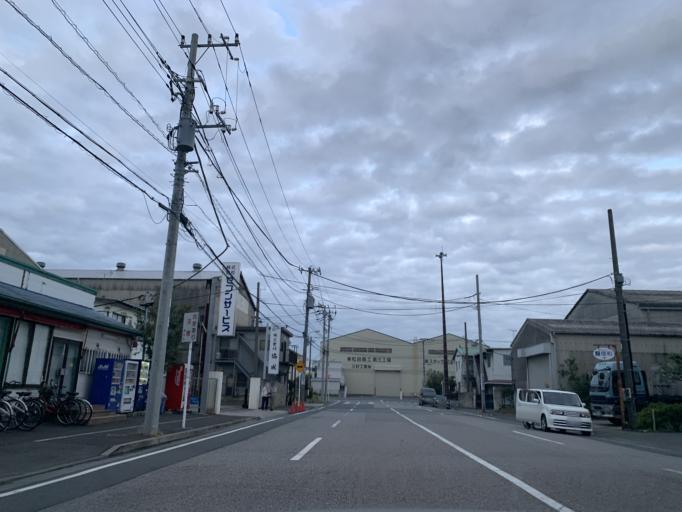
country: JP
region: Tokyo
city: Urayasu
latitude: 35.6309
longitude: 139.8937
